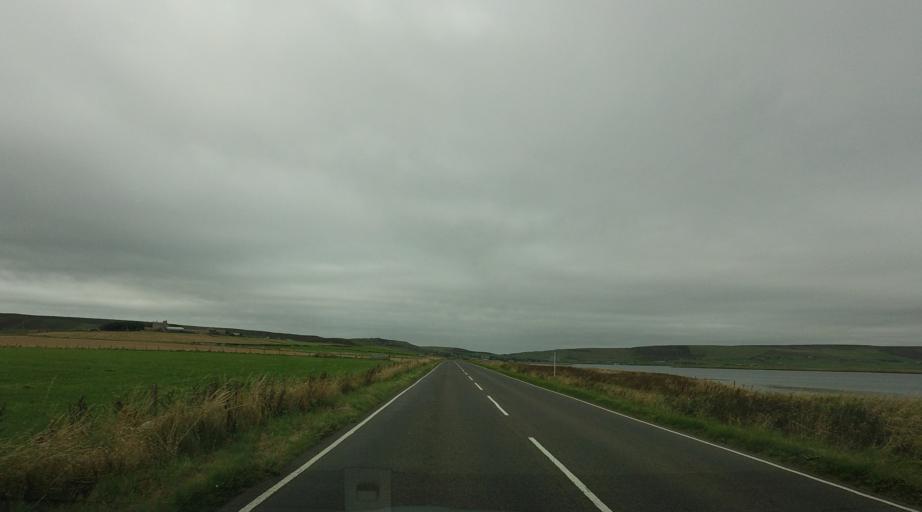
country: GB
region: Scotland
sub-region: Orkney Islands
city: Orkney
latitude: 58.9958
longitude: -3.0702
